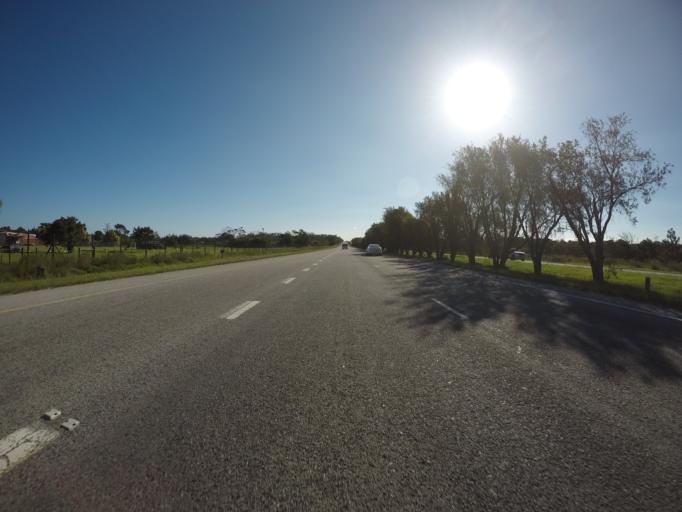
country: ZA
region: Eastern Cape
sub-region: Nelson Mandela Bay Metropolitan Municipality
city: Port Elizabeth
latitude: -33.9460
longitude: 25.4000
